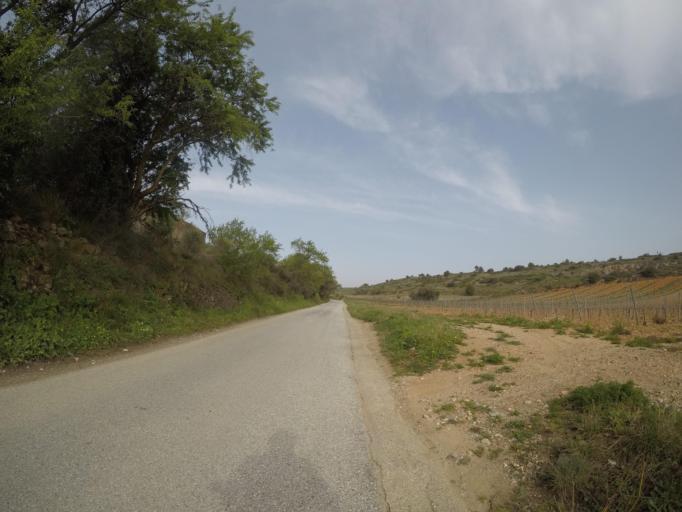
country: FR
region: Languedoc-Roussillon
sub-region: Departement des Pyrenees-Orientales
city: Baixas
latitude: 42.7658
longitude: 2.8147
